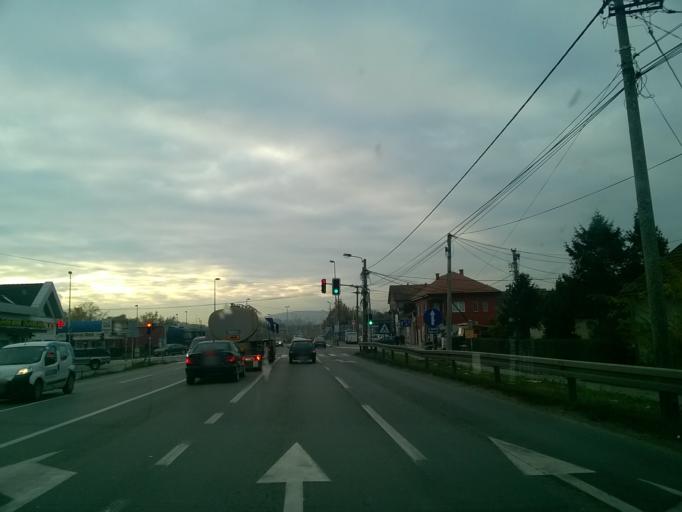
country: RS
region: Central Serbia
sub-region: Belgrade
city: Stari Grad
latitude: 44.8402
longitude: 20.4915
